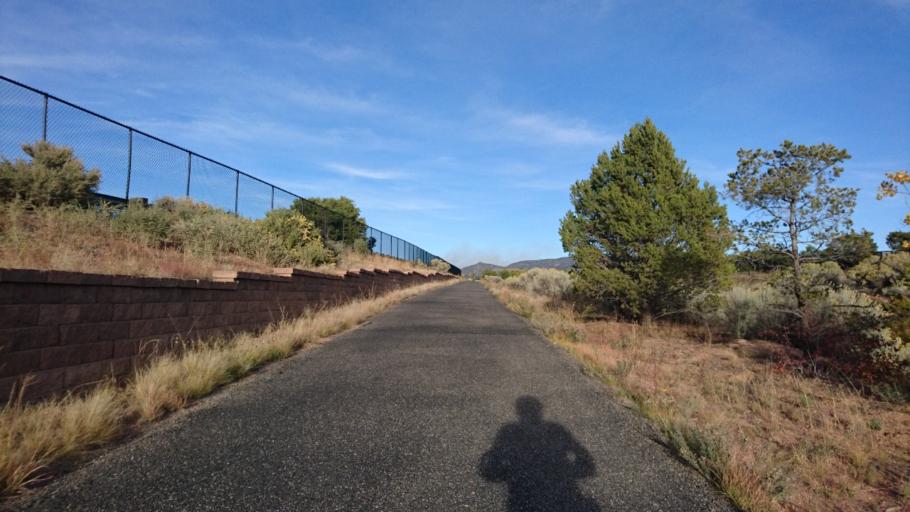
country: US
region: New Mexico
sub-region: Santa Fe County
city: Santa Fe
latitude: 35.6478
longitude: -105.9681
